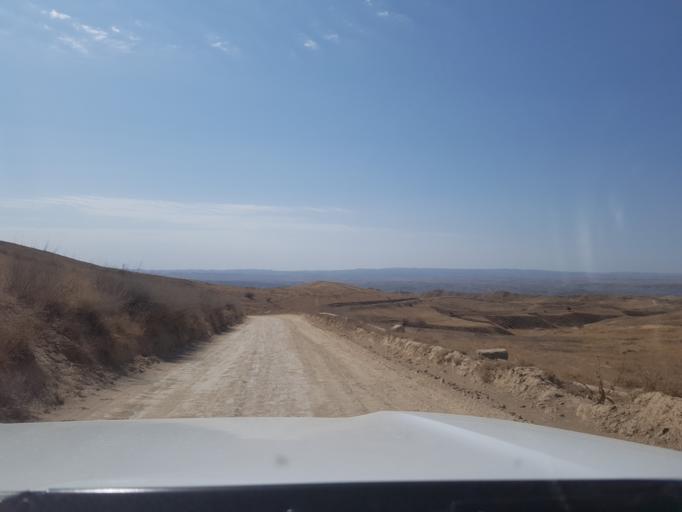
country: TM
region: Ahal
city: Baharly
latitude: 38.2723
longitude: 56.8954
